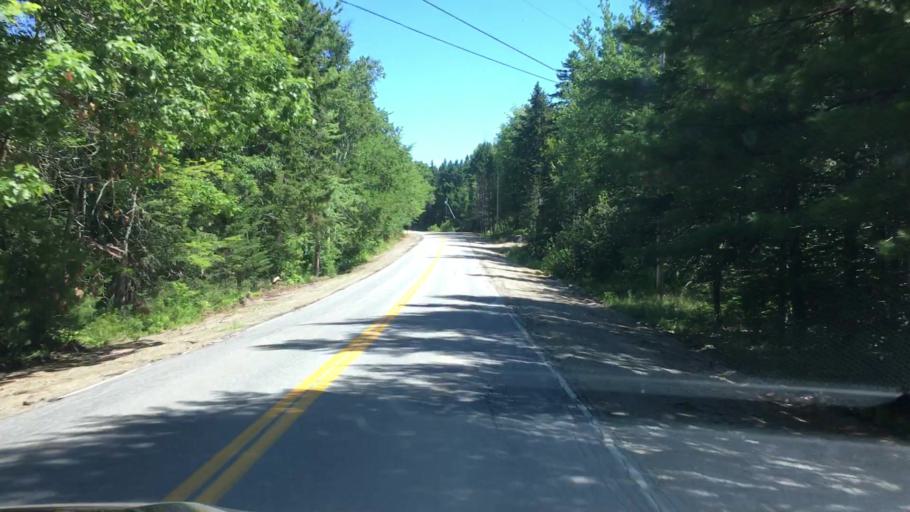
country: US
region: Maine
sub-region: Hancock County
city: Penobscot
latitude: 44.4443
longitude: -68.7035
